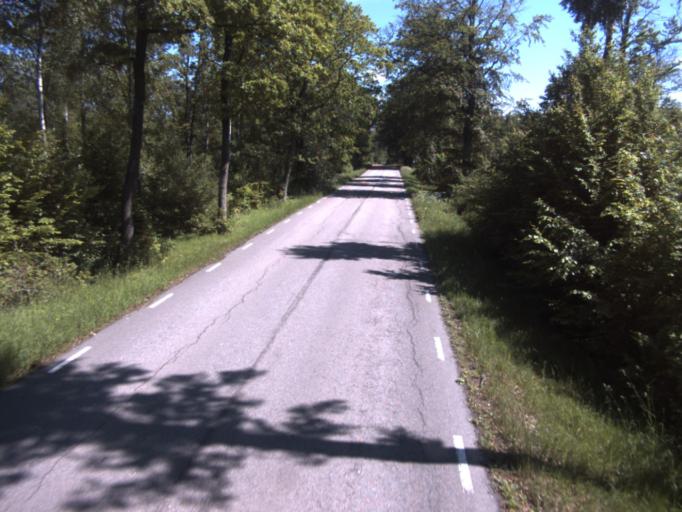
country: SE
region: Skane
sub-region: Helsingborg
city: Odakra
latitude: 56.1105
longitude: 12.6648
